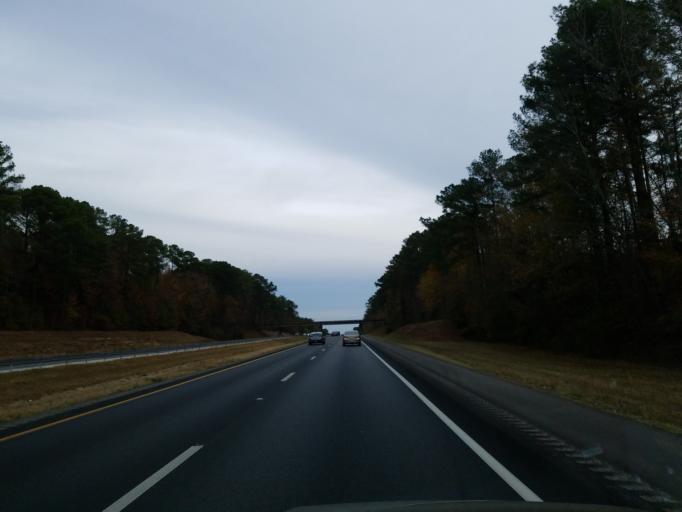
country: US
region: Mississippi
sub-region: Lauderdale County
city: Marion
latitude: 32.3901
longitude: -88.5986
